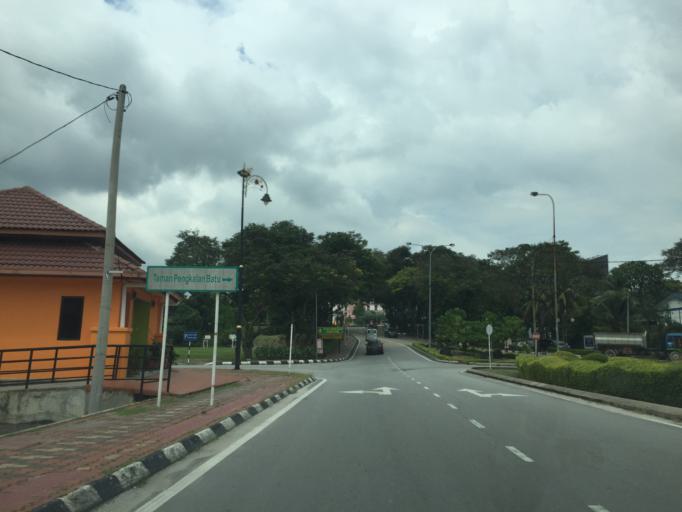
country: MY
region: Selangor
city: Klang
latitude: 3.0423
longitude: 101.4464
